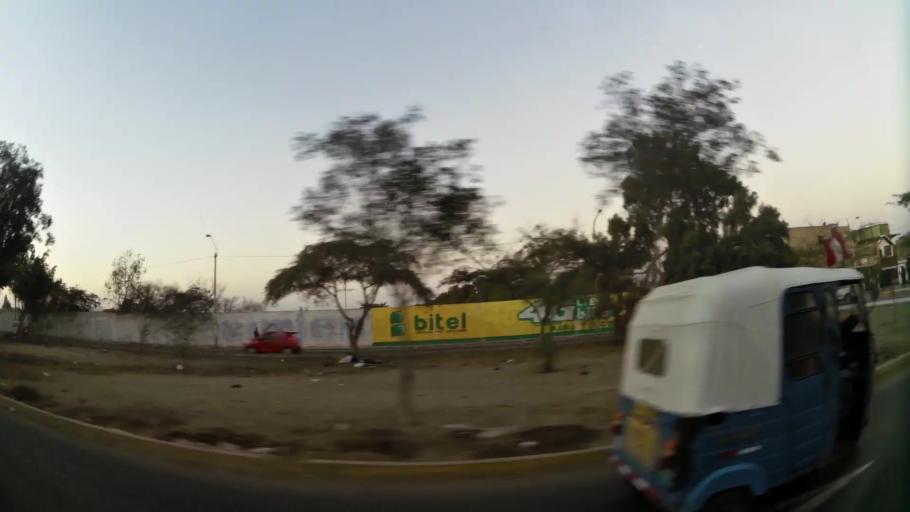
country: PE
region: Ica
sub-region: Provincia de Ica
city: Ica
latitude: -14.0816
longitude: -75.7301
